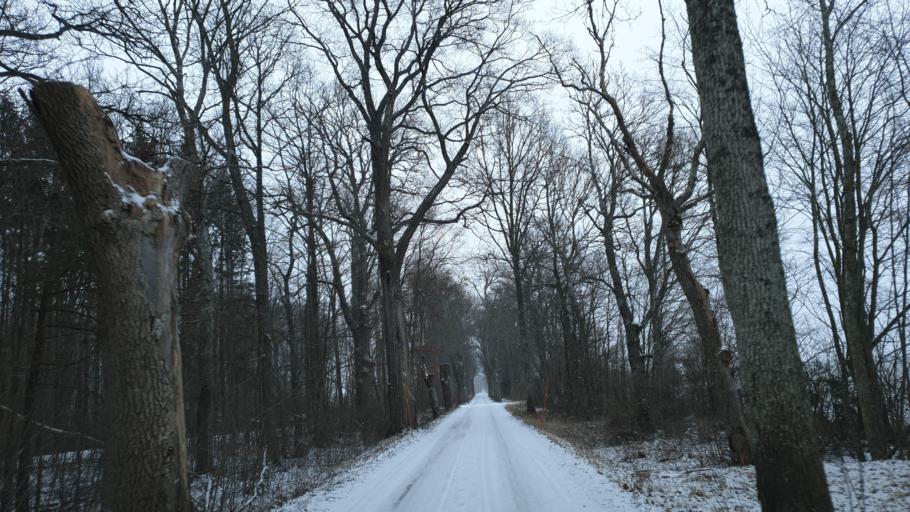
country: SE
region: Gotland
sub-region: Gotland
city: Visby
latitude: 57.5224
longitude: 18.4504
